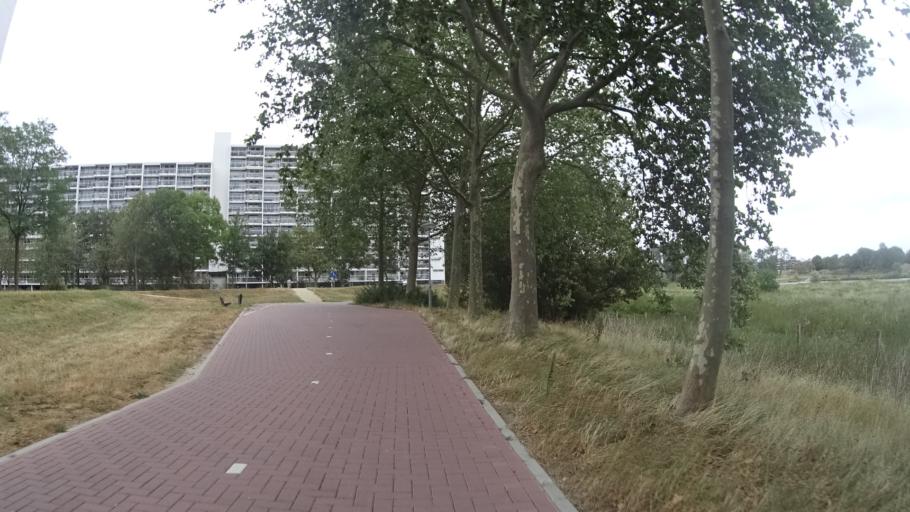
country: NL
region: Limburg
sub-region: Gemeente Venlo
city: Tegelen
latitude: 51.3601
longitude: 6.1474
